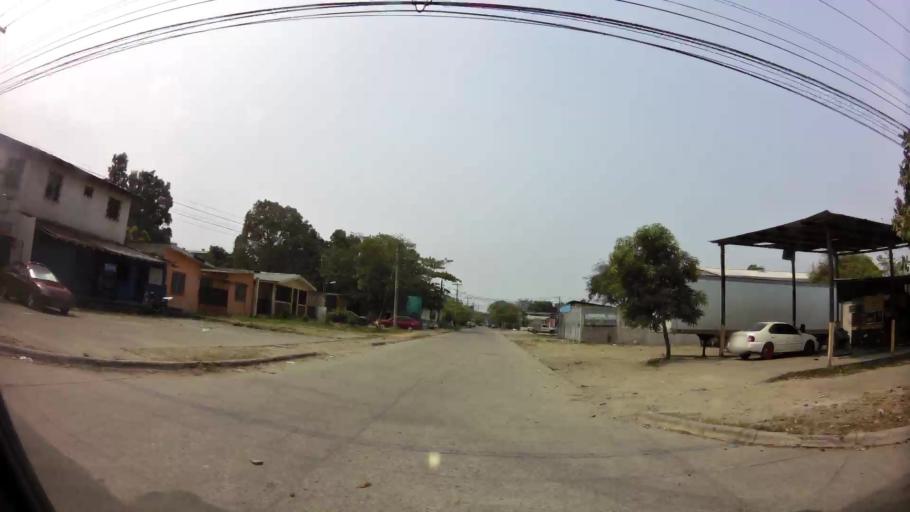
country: HN
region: Cortes
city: San Pedro Sula
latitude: 15.4871
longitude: -88.0209
